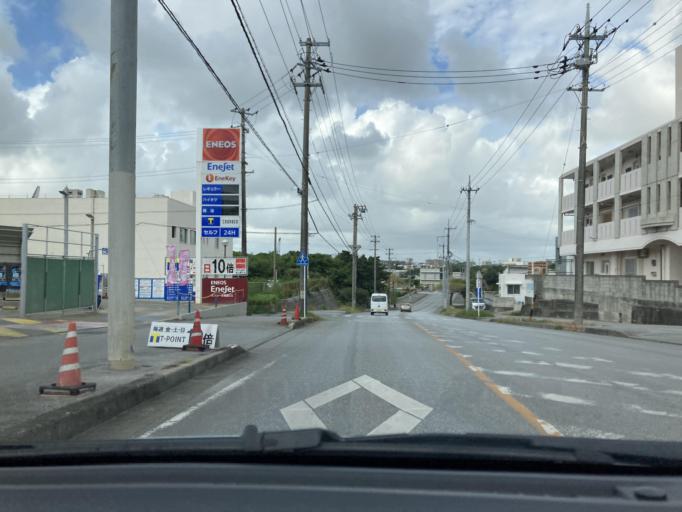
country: JP
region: Okinawa
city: Itoman
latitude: 26.1351
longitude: 127.6870
